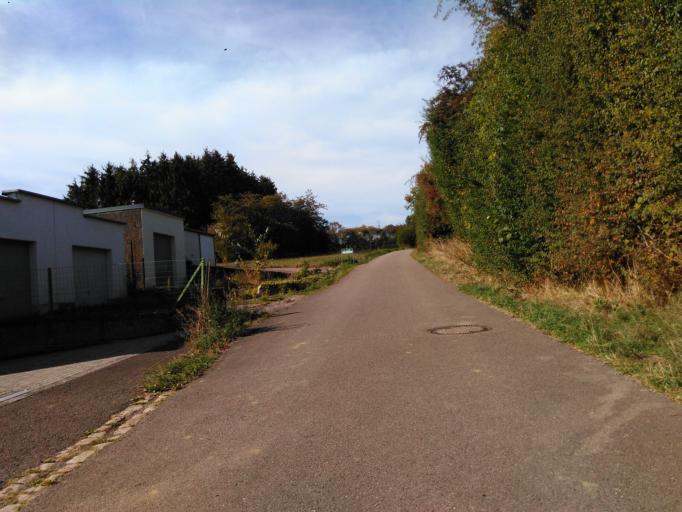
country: LU
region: Luxembourg
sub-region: Canton d'Esch-sur-Alzette
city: Petange
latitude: 49.5630
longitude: 5.8802
